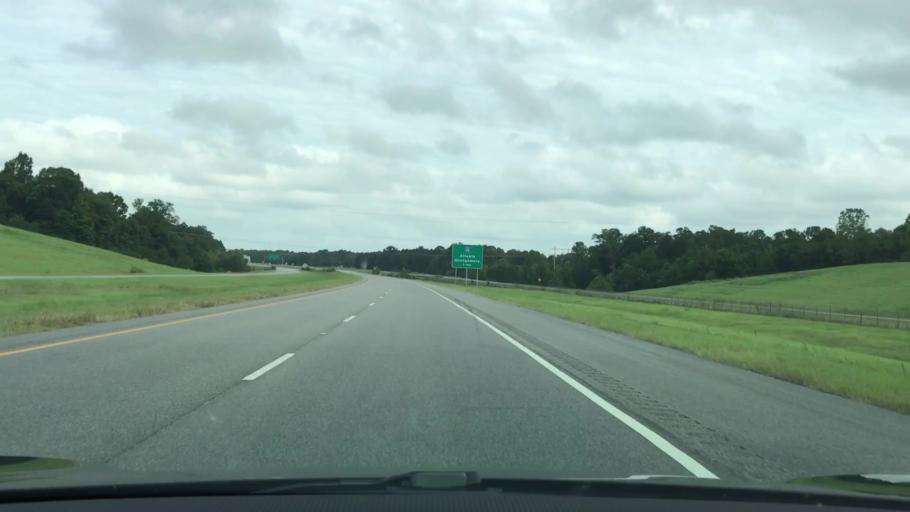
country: US
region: Alabama
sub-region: Montgomery County
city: Pike Road
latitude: 32.3514
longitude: -86.0663
